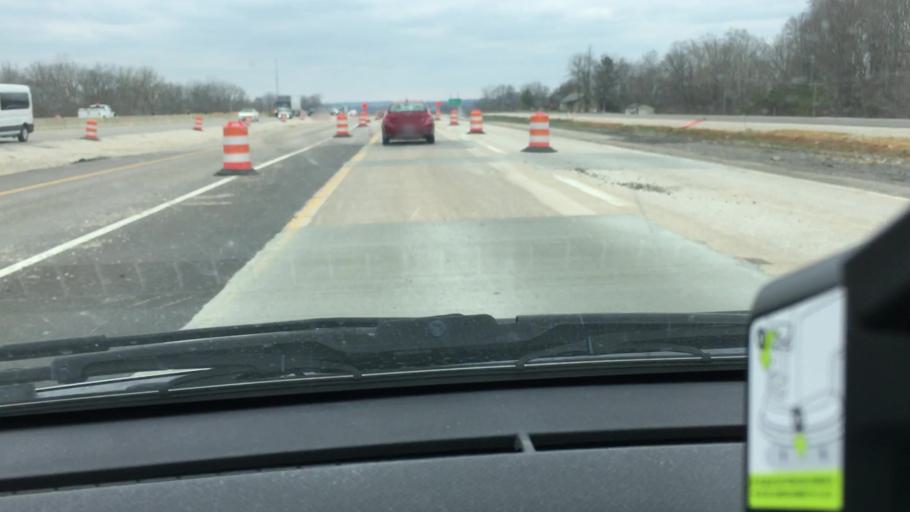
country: US
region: Indiana
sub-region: Monroe County
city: Bloomington
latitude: 39.2570
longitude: -86.5258
